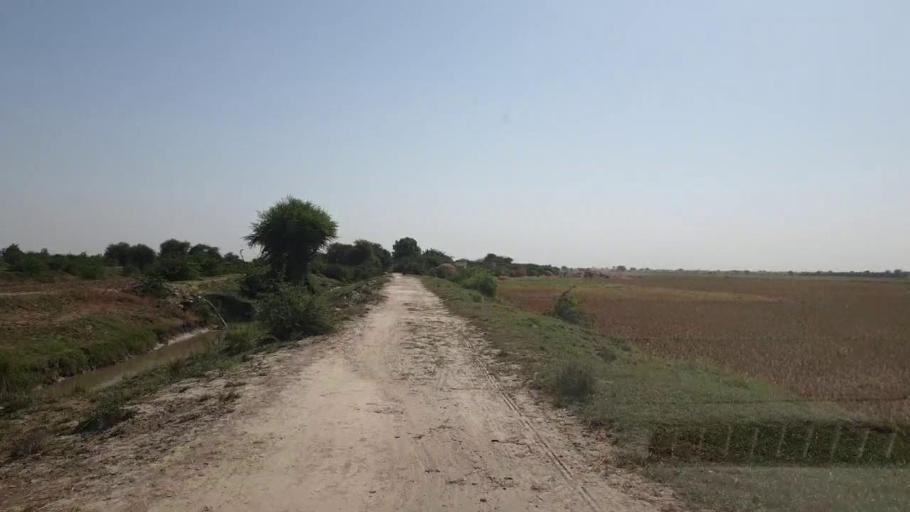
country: PK
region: Sindh
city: Kadhan
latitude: 24.6304
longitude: 68.9933
